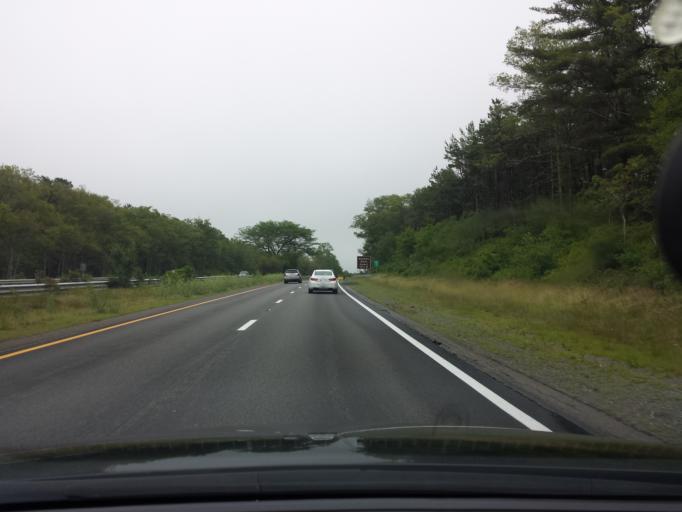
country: US
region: Massachusetts
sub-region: Barnstable County
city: Sagamore
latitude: 41.7537
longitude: -70.5189
